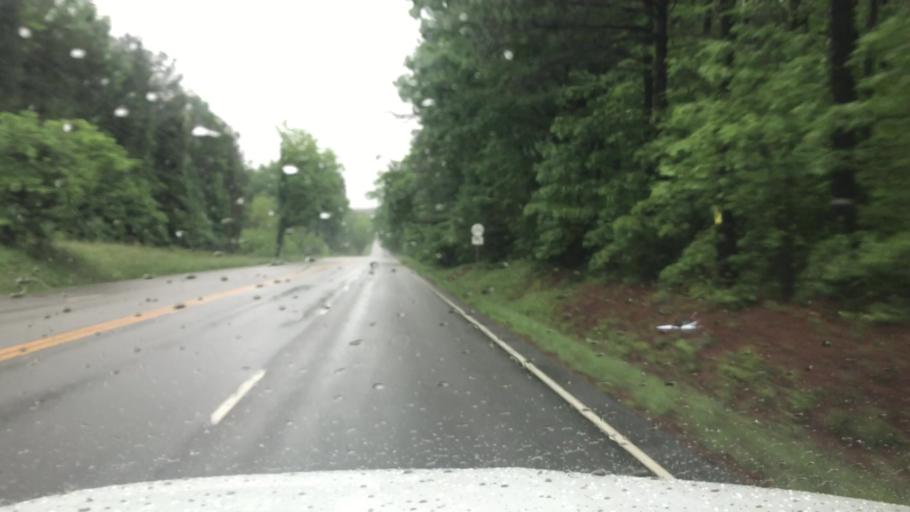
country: US
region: Virginia
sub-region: Hanover County
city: Ashland
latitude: 37.8256
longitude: -77.4714
